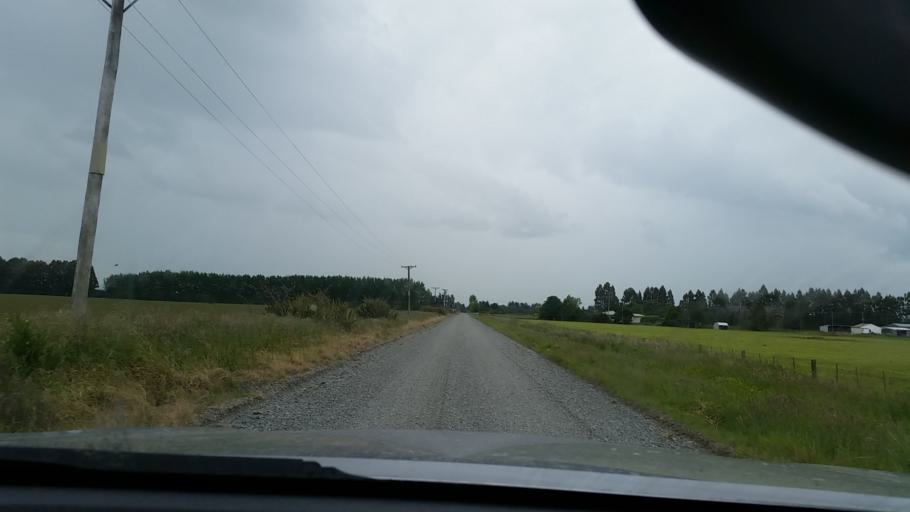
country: NZ
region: Southland
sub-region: Southland District
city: Winton
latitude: -46.0069
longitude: 168.1793
